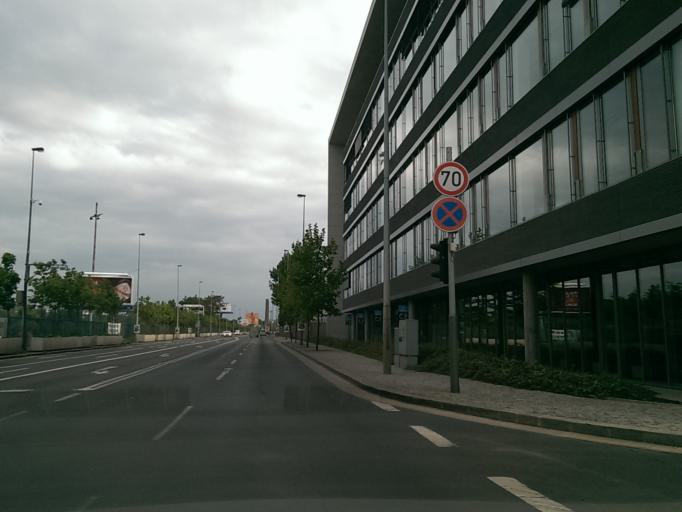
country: CZ
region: Praha
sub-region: Praha 2
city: Vysehrad
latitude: 50.0602
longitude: 14.4110
